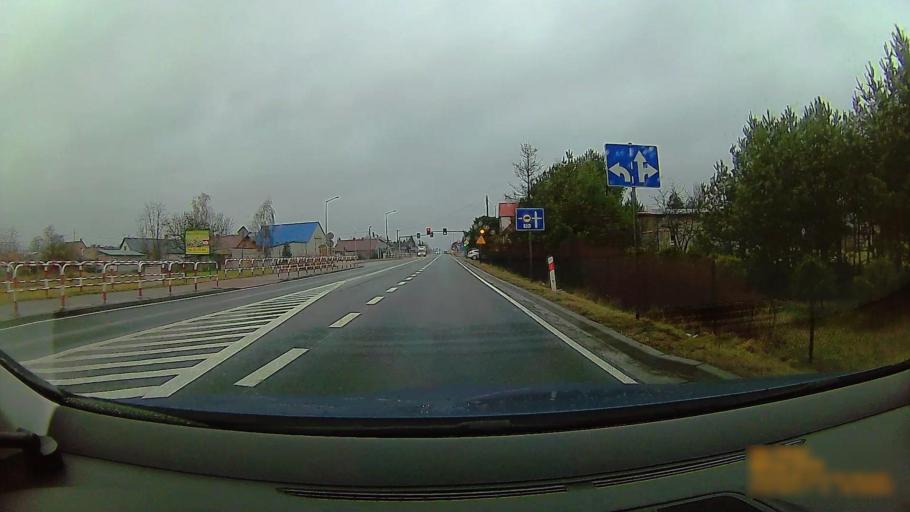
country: PL
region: Greater Poland Voivodeship
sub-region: Konin
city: Konin
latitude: 52.1751
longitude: 18.2720
